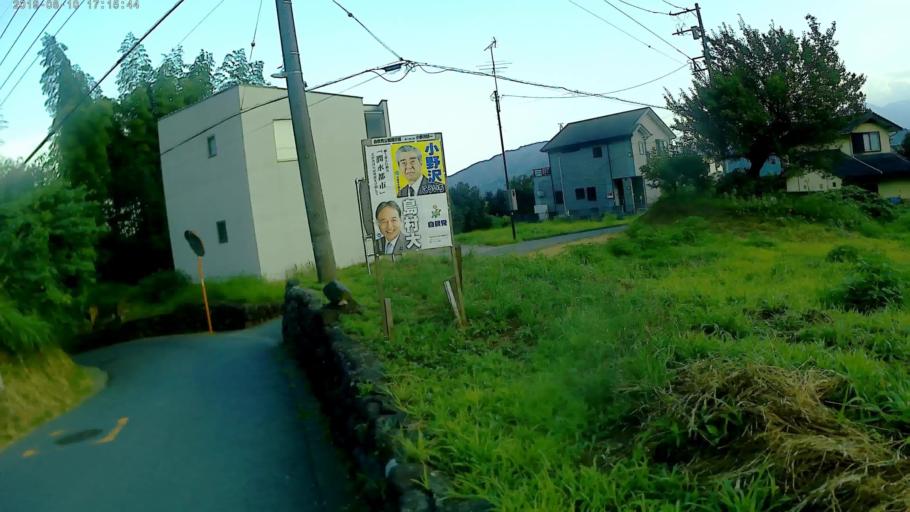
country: JP
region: Yamanashi
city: Uenohara
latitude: 35.6242
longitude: 139.1711
